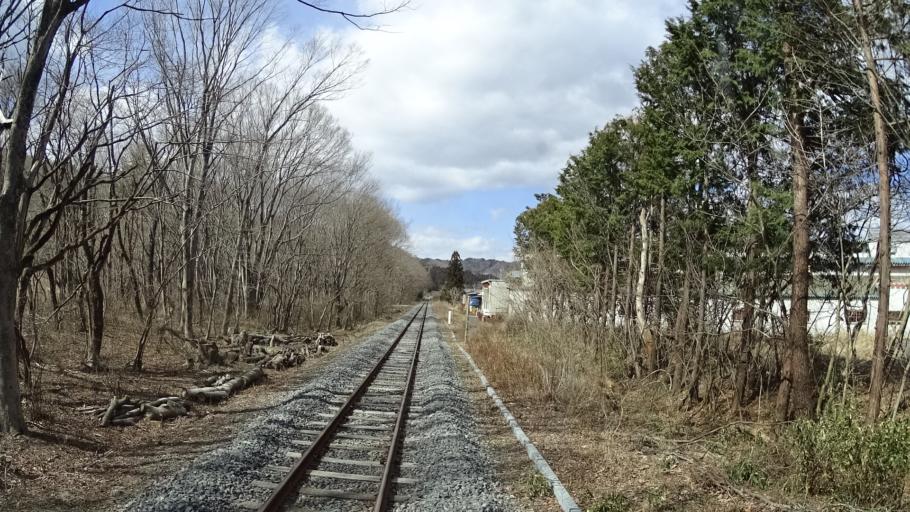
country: JP
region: Iwate
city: Miyako
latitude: 39.5580
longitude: 141.9389
